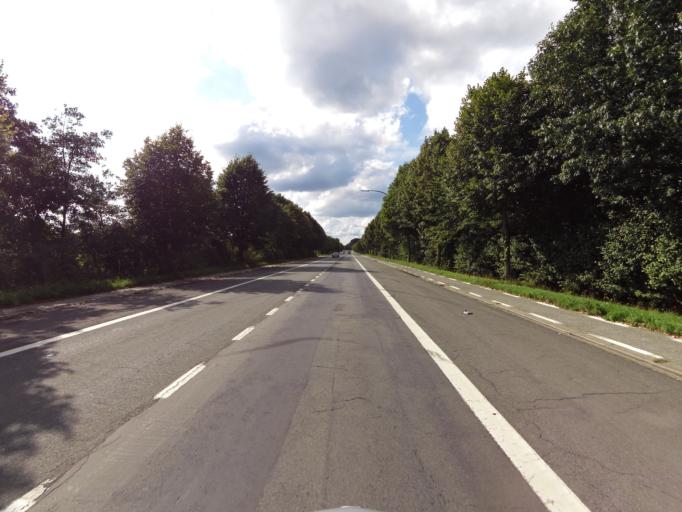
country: BE
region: Flanders
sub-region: Provincie Oost-Vlaanderen
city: Ronse
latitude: 50.7642
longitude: 3.5522
